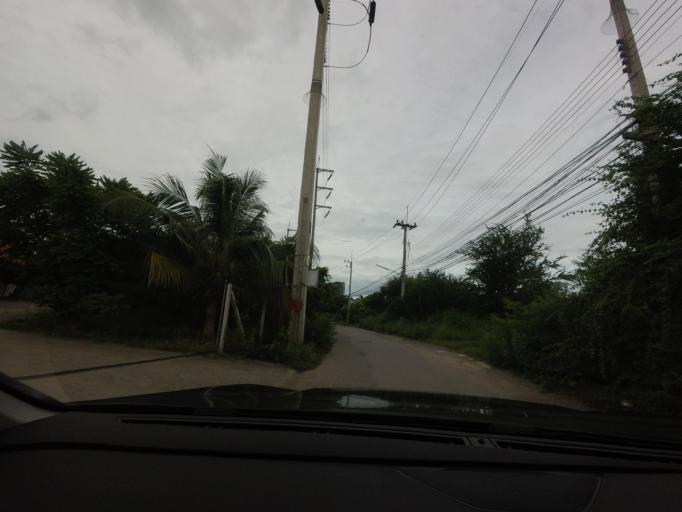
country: TH
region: Prachuap Khiri Khan
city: Hua Hin
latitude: 12.5379
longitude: 99.9513
